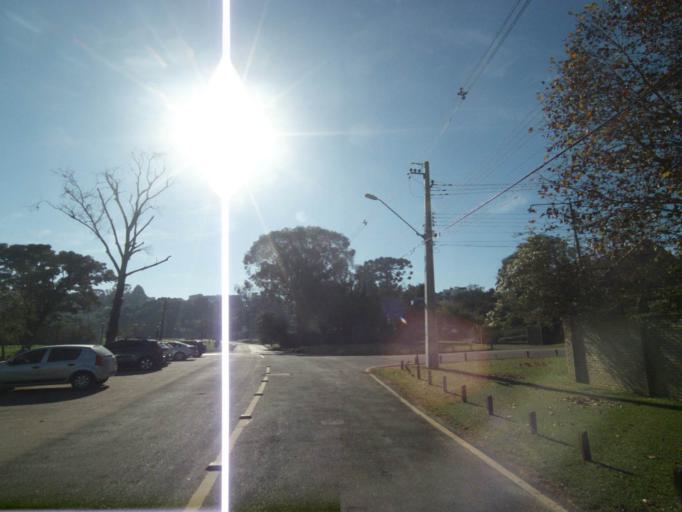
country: BR
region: Parana
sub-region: Curitiba
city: Curitiba
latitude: -25.4291
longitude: -49.3061
